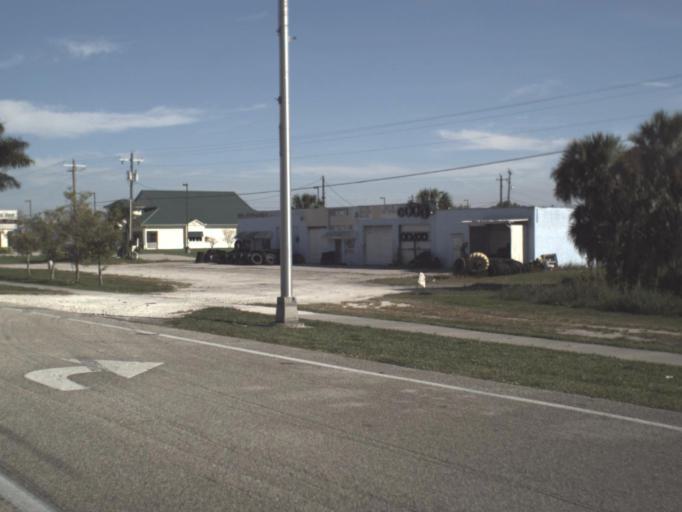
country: US
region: Florida
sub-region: Glades County
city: Moore Haven
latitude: 26.8337
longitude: -81.1087
